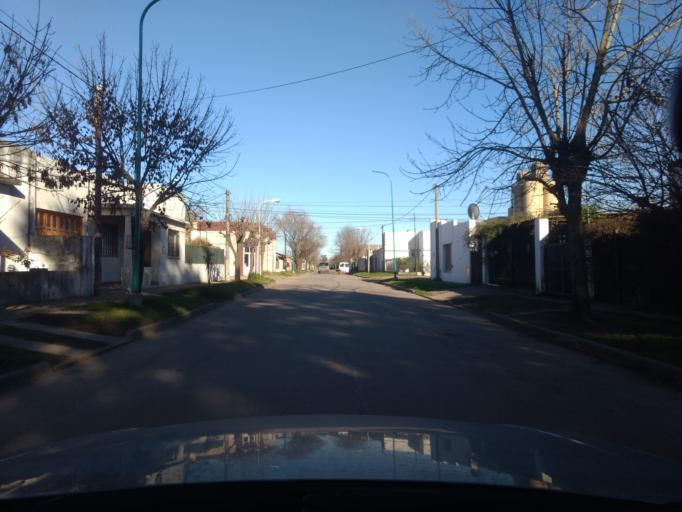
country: AR
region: Buenos Aires
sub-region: Partido de Navarro
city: Navarro
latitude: -35.0004
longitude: -59.2763
